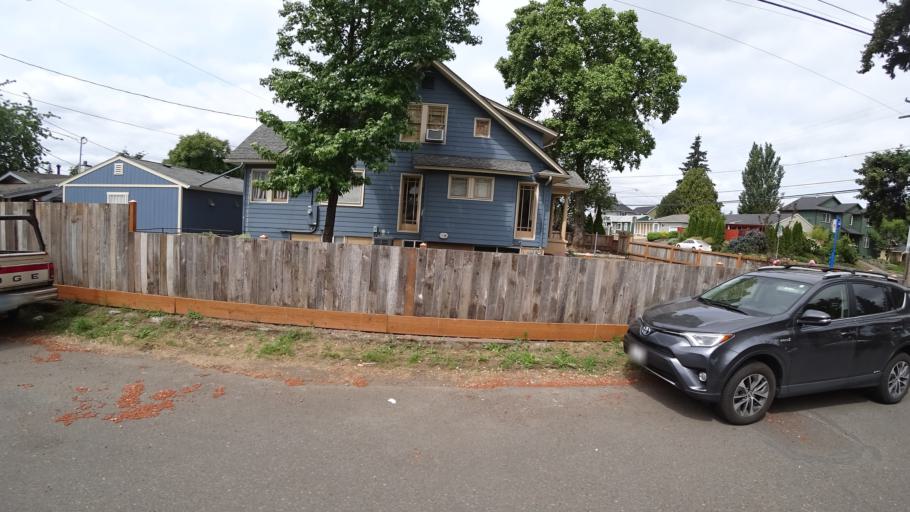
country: US
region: Oregon
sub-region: Multnomah County
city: Lents
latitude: 45.4757
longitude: -122.5865
